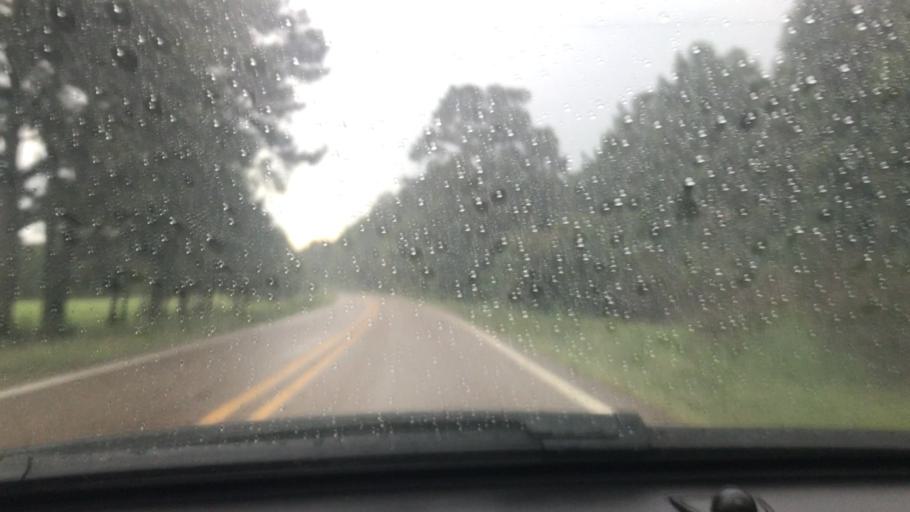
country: US
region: Mississippi
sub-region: Pike County
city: Summit
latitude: 31.2924
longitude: -90.4972
